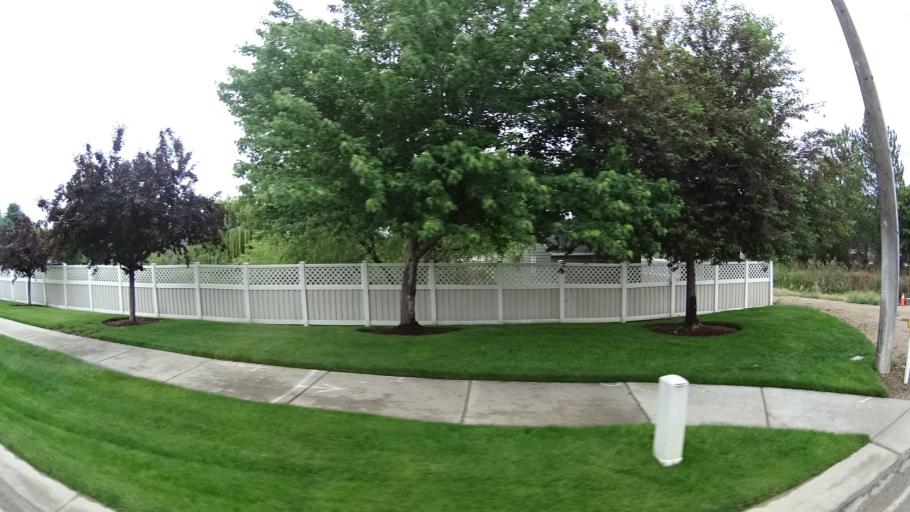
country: US
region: Idaho
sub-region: Ada County
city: Star
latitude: 43.6965
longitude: -116.4733
